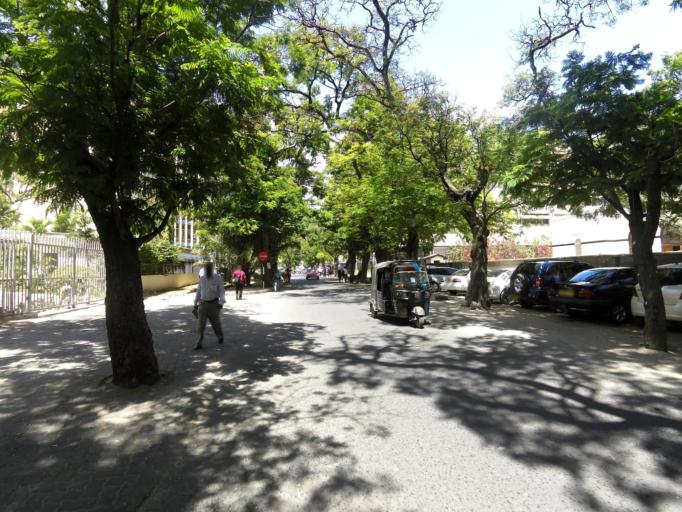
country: TZ
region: Dar es Salaam
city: Dar es Salaam
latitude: -6.8158
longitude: 39.2926
